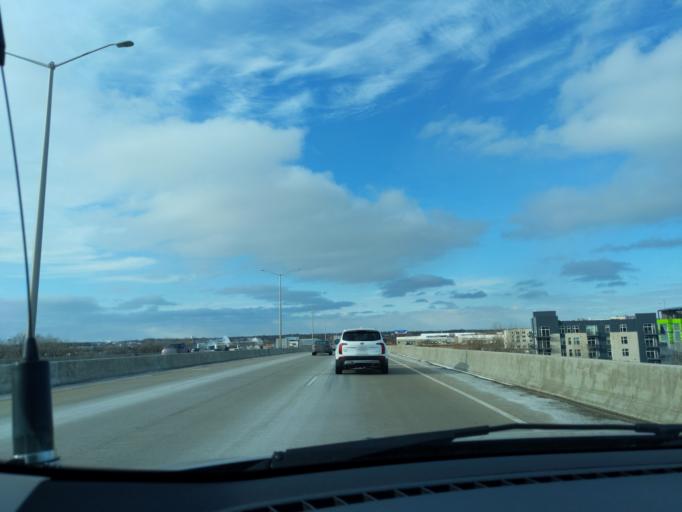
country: US
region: Wisconsin
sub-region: Brown County
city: Ashwaubenon
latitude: 44.4763
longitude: -88.0470
